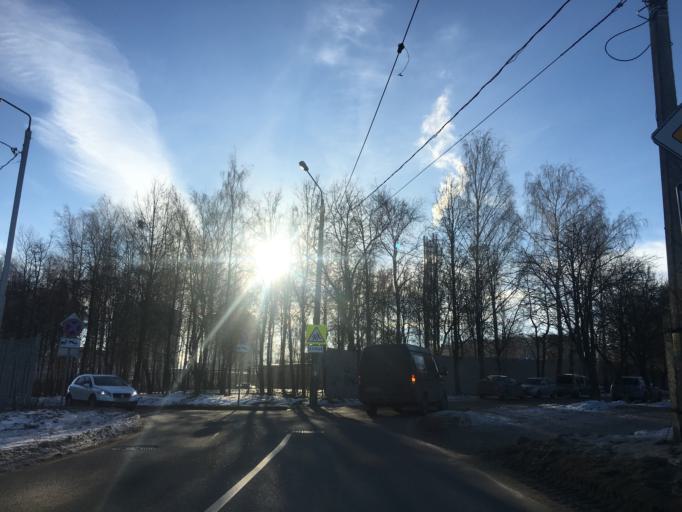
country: RU
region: Tula
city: Mendeleyevskiy
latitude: 54.1776
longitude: 37.5778
